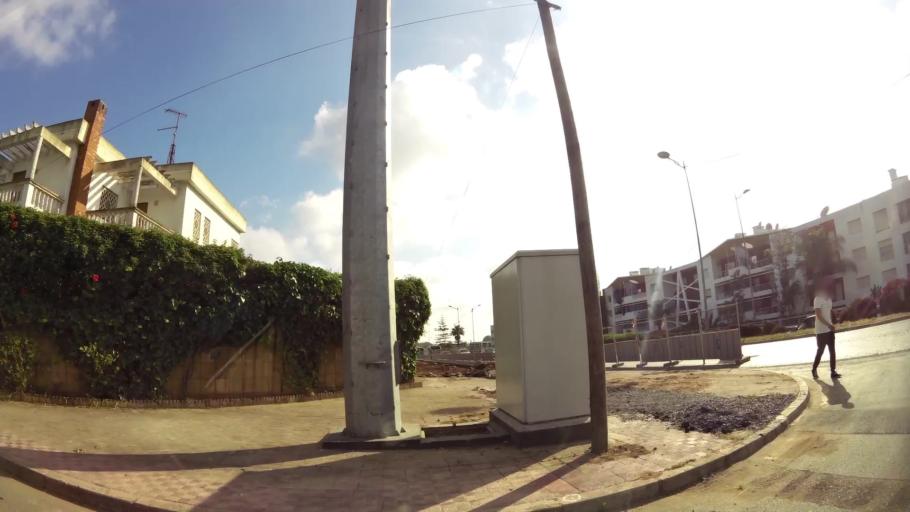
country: MA
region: Rabat-Sale-Zemmour-Zaer
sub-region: Skhirate-Temara
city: Temara
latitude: 33.9507
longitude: -6.8671
